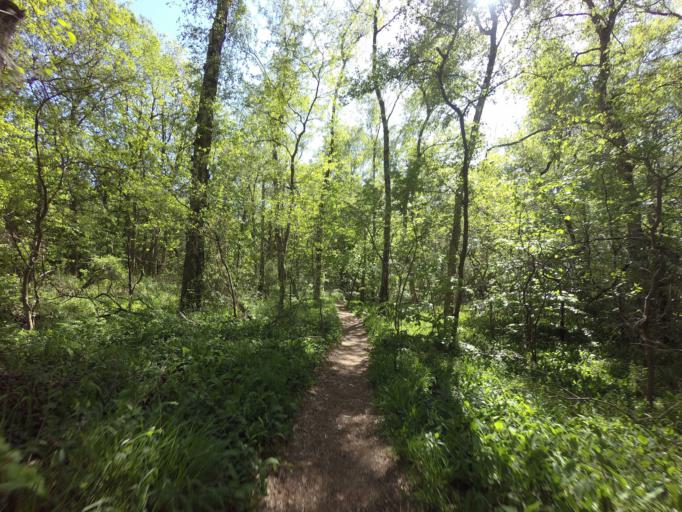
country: DE
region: Lower Saxony
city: Lehre
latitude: 52.2978
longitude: 10.6669
